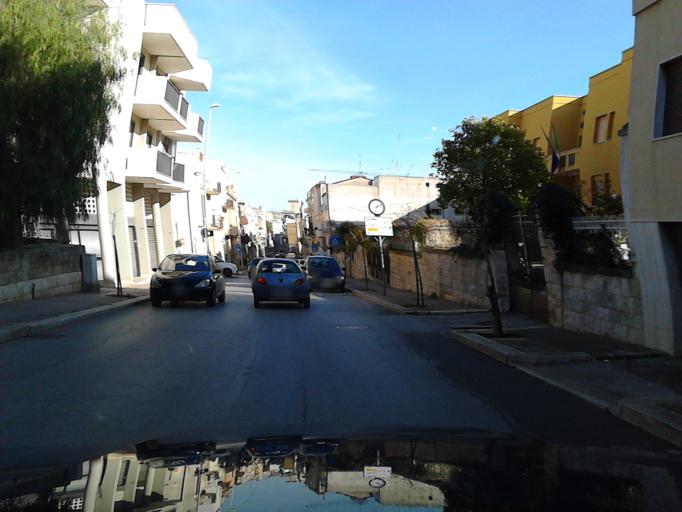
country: IT
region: Apulia
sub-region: Provincia di Bari
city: Rutigliano
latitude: 41.0092
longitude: 16.9992
